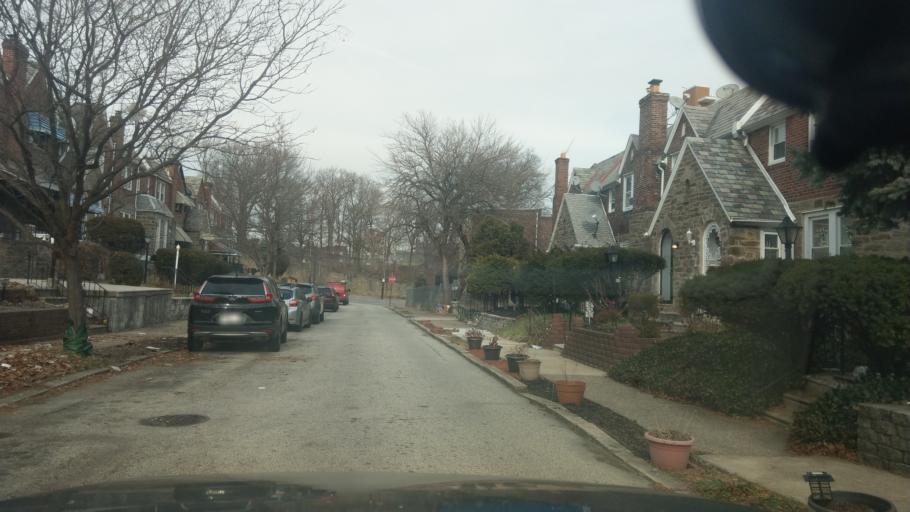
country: US
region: Pennsylvania
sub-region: Montgomery County
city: Wyncote
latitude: 40.0487
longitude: -75.1467
